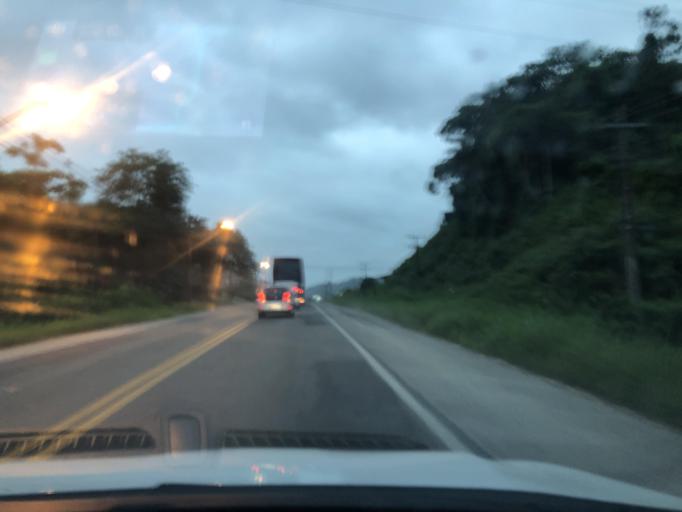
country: BR
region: Santa Catarina
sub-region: Pomerode
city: Pomerode
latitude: -26.7821
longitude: -49.0843
